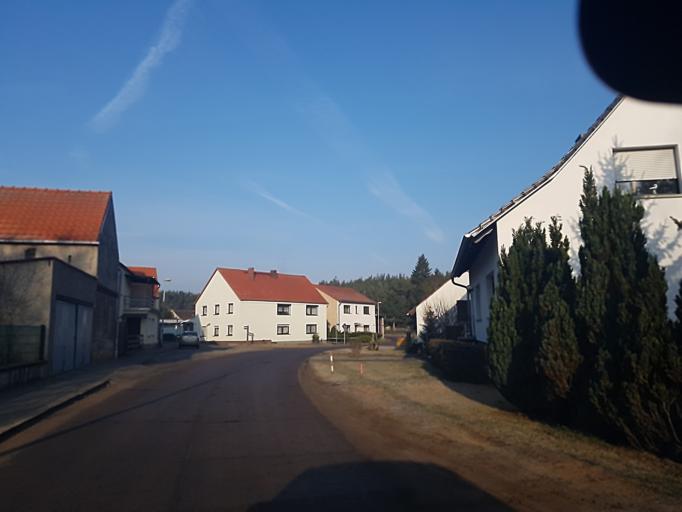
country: DE
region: Brandenburg
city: Golzow
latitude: 52.2435
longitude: 12.5682
